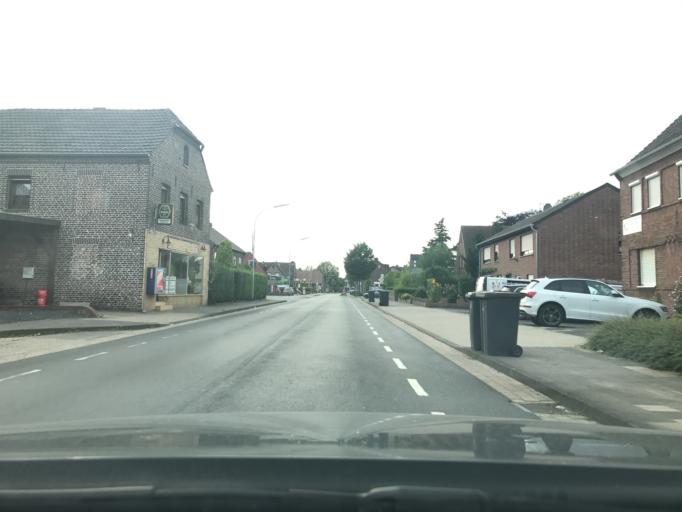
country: DE
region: North Rhine-Westphalia
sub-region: Regierungsbezirk Dusseldorf
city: Wachtendonk
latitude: 51.4084
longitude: 6.3420
